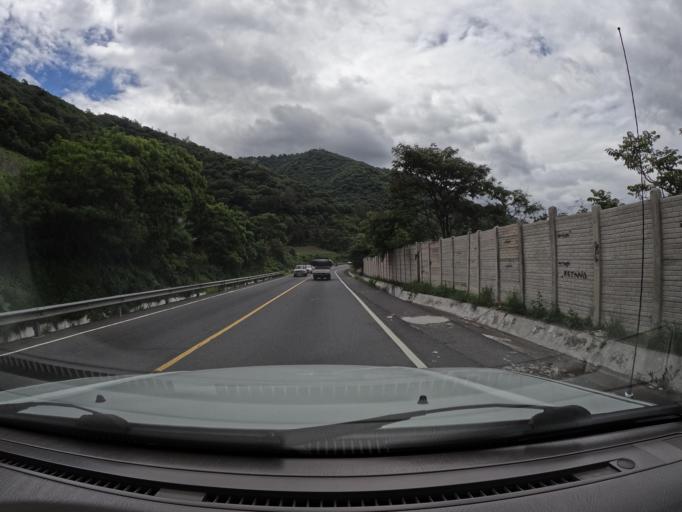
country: GT
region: Sacatepequez
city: San Antonio Aguas Calientes
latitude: 14.5488
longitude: -90.7591
